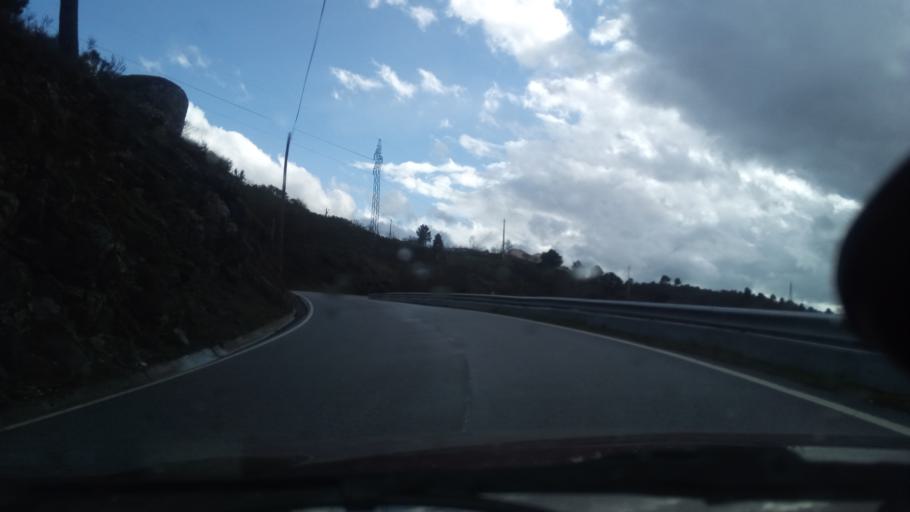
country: PT
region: Guarda
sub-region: Guarda
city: Guarda
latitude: 40.5467
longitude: -7.3232
